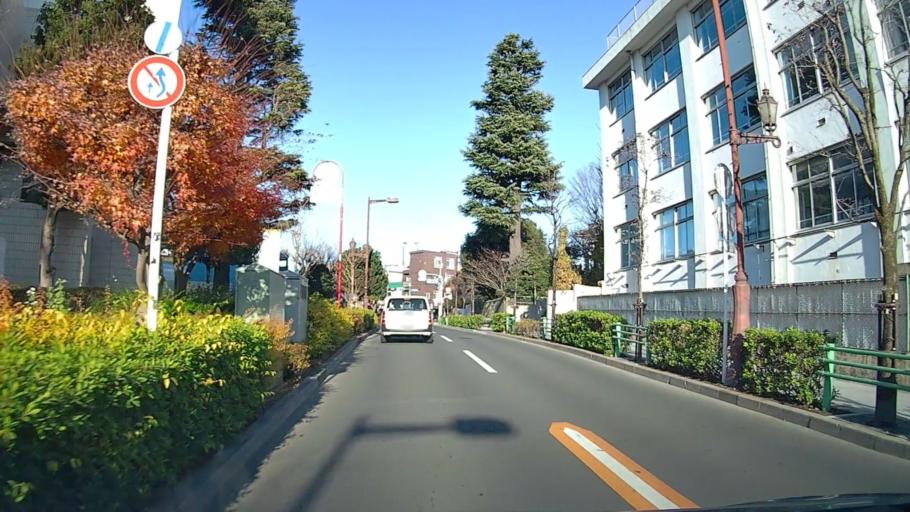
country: JP
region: Tokyo
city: Tokyo
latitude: 35.7041
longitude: 139.6721
